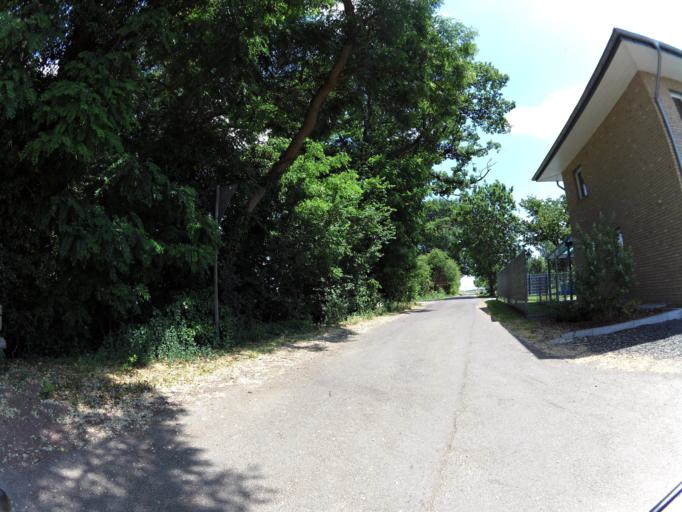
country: DE
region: North Rhine-Westphalia
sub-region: Regierungsbezirk Koln
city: Heinsberg
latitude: 51.0176
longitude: 6.0923
